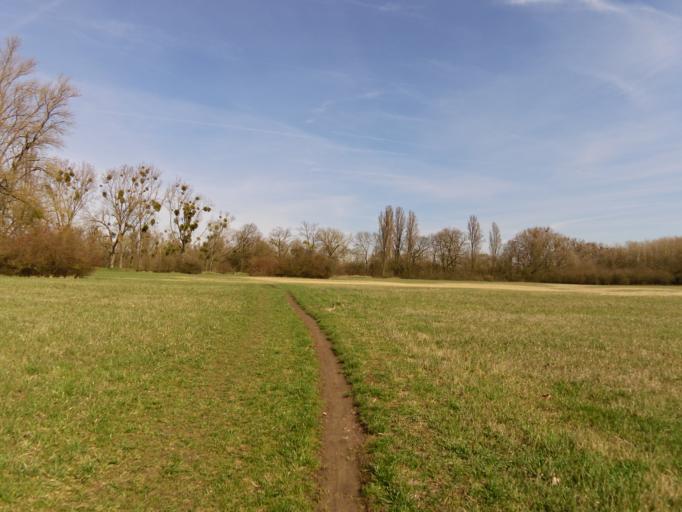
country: DE
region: Rheinland-Pfalz
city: Gimbsheim
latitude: 49.8110
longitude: 8.3976
